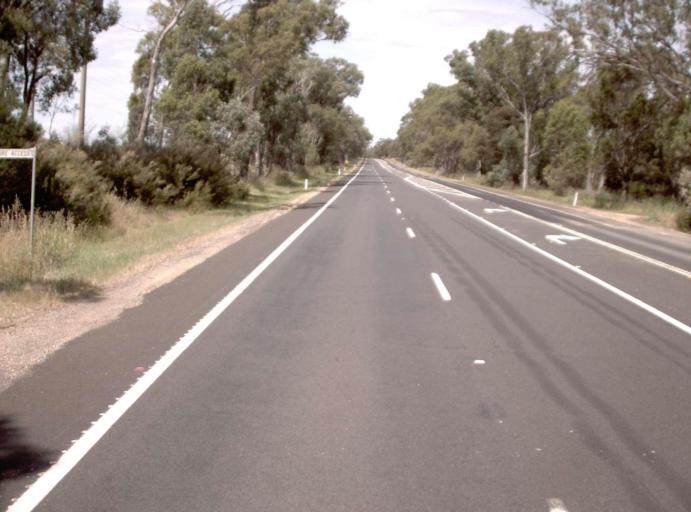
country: AU
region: Victoria
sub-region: Wellington
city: Sale
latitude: -37.9311
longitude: 147.1938
